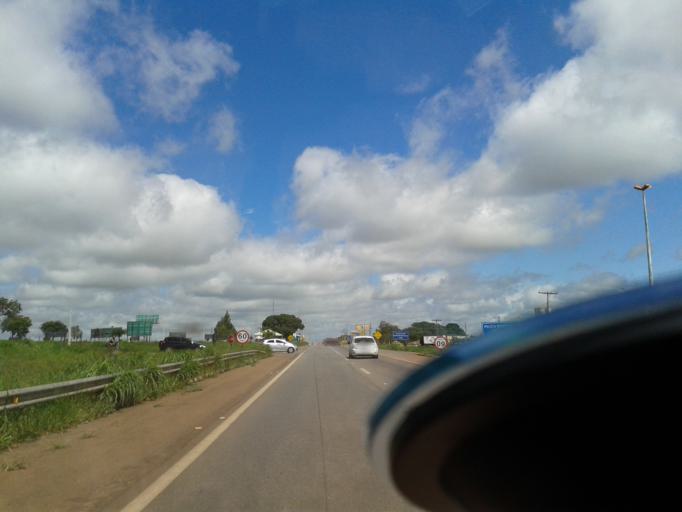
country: BR
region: Goias
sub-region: Goiania
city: Goiania
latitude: -16.6214
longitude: -49.3561
